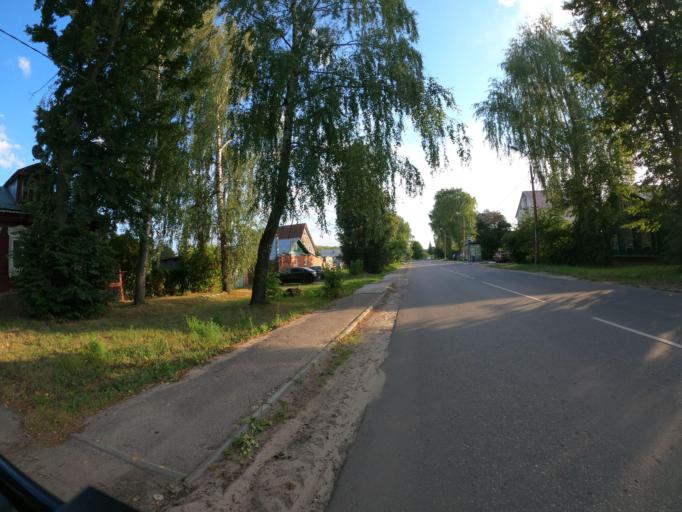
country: RU
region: Moskovskaya
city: Raduzhnyy
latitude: 55.1029
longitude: 38.7340
